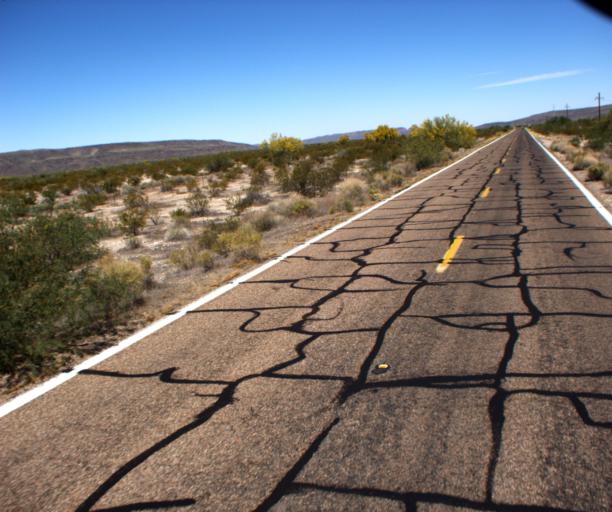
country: US
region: Arizona
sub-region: Pima County
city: Ajo
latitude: 32.4364
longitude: -112.8711
